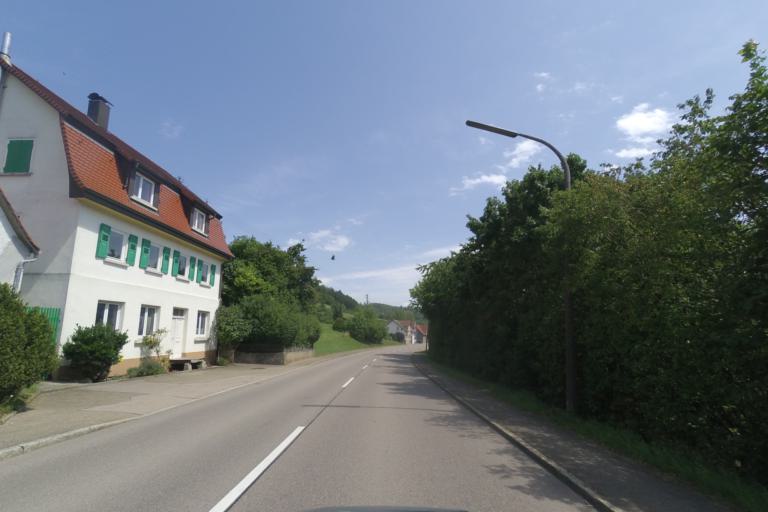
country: DE
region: Baden-Wuerttemberg
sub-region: Regierungsbezirk Stuttgart
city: Gaildorf
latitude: 48.9776
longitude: 9.8045
